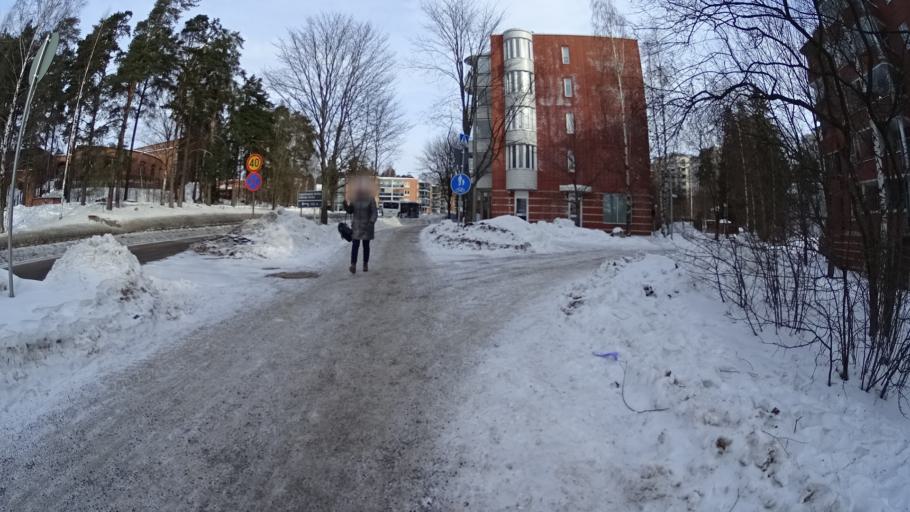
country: FI
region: Uusimaa
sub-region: Helsinki
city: Kilo
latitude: 60.2254
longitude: 24.8116
